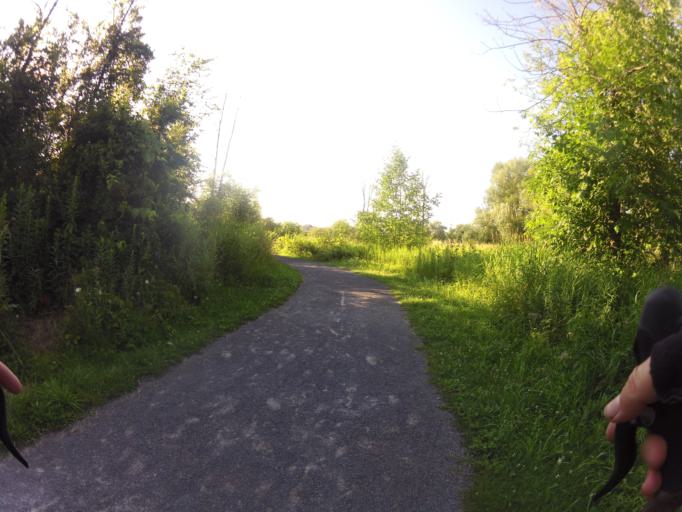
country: CA
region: Ontario
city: Bells Corners
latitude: 45.2712
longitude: -75.7025
